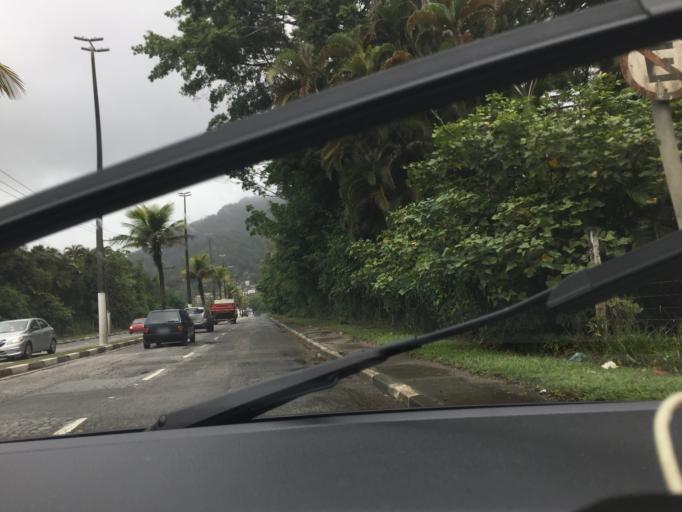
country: BR
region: Sao Paulo
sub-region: Guaruja
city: Guaruja
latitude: -23.9704
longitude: -46.2580
